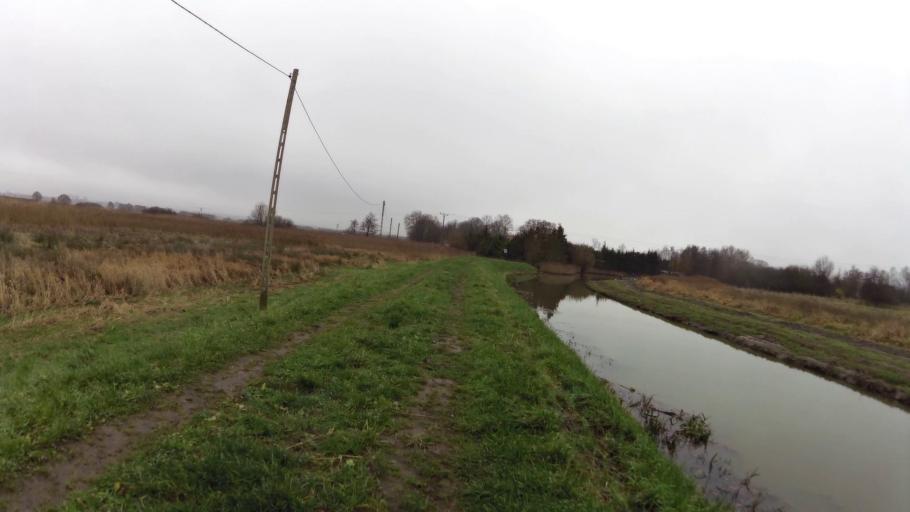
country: PL
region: West Pomeranian Voivodeship
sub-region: Powiat koszalinski
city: Mielno
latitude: 54.2458
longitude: 16.0817
